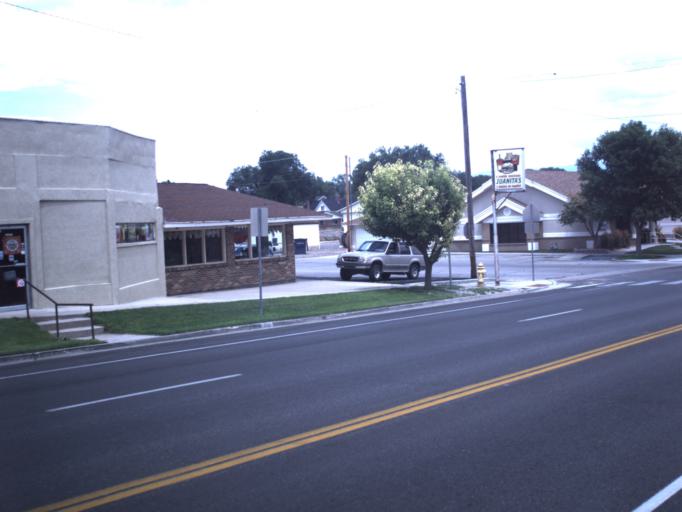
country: US
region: Utah
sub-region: Sanpete County
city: Moroni
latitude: 39.5249
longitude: -111.5863
